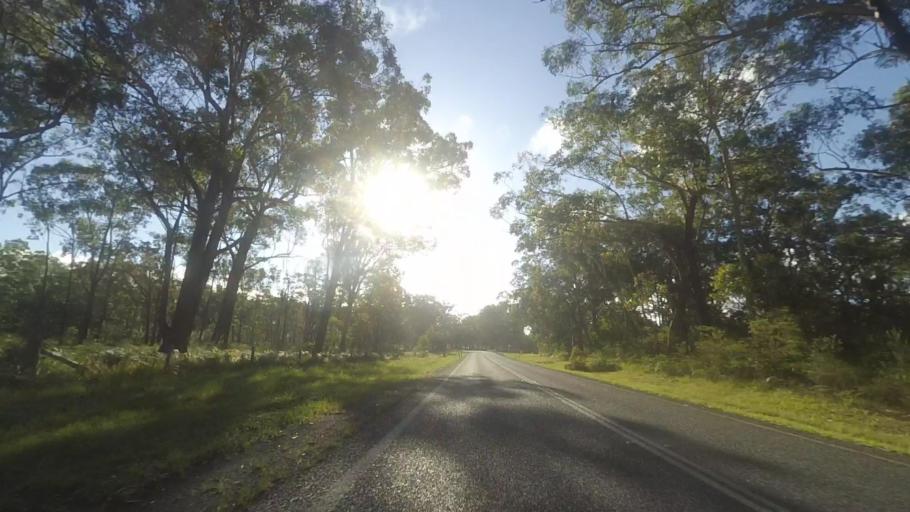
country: AU
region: New South Wales
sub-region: Great Lakes
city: Nabiac
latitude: -32.0909
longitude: 152.4593
